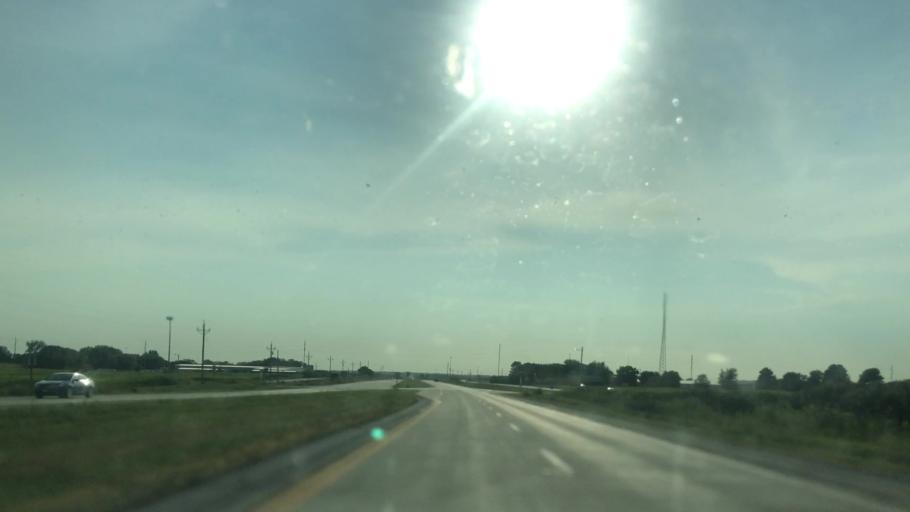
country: US
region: Iowa
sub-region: Story County
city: Ames
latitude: 42.0089
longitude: -93.5536
